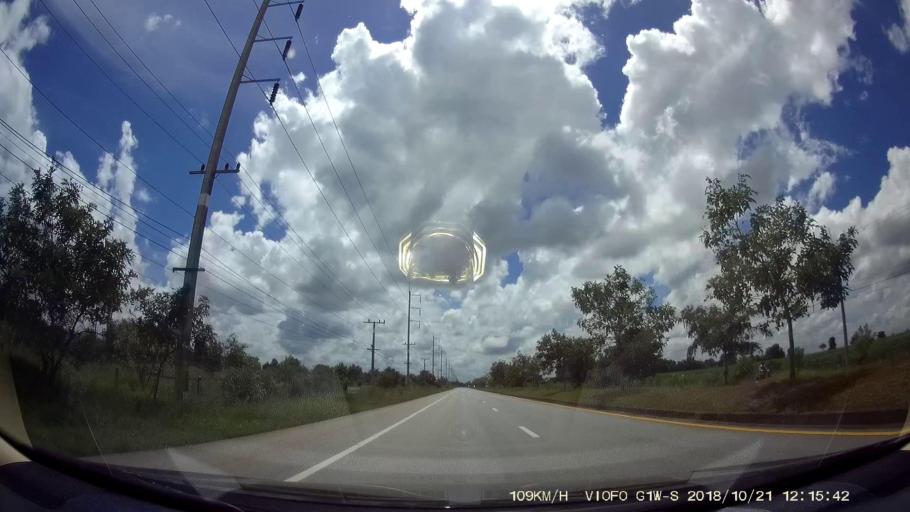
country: TH
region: Nakhon Ratchasima
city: Dan Khun Thot
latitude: 15.3587
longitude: 101.8293
